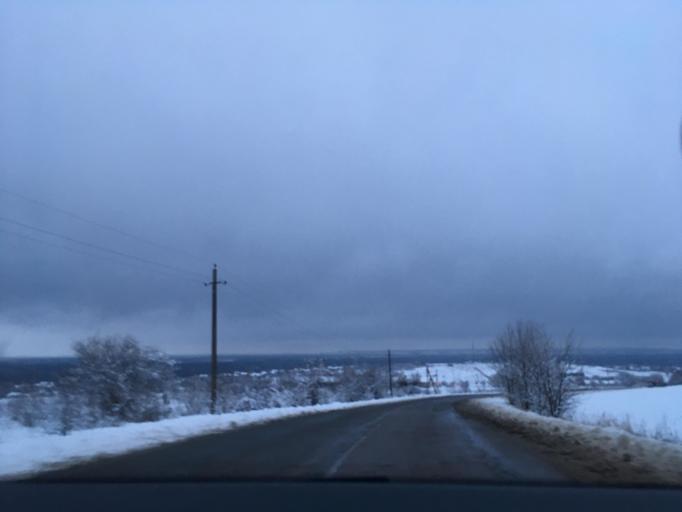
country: RU
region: Voronezj
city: Verkhniy Mamon
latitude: 50.0723
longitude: 40.2900
